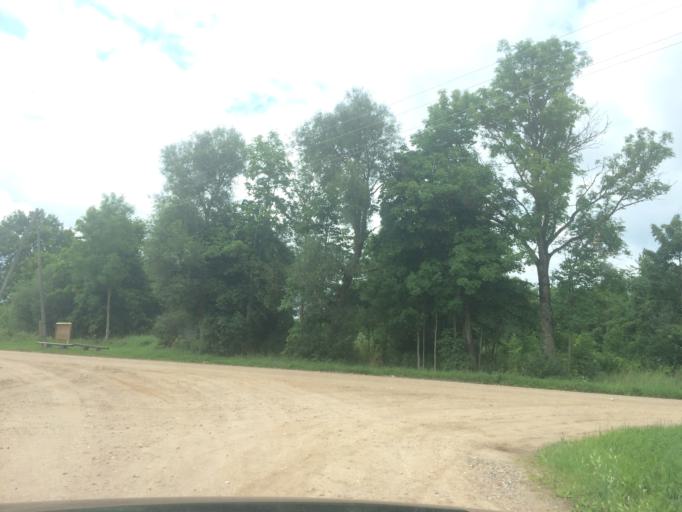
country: LV
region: Rezekne
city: Rezekne
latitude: 56.6631
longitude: 27.2696
